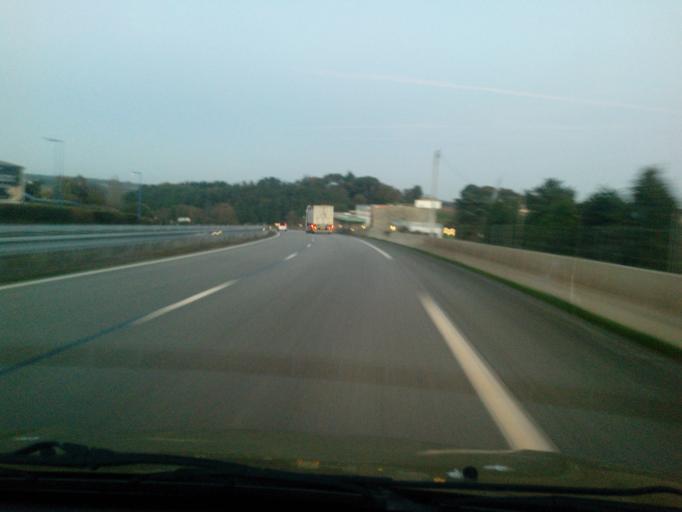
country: FR
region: Brittany
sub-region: Departement du Morbihan
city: Guegon
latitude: 47.9467
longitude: -2.5838
